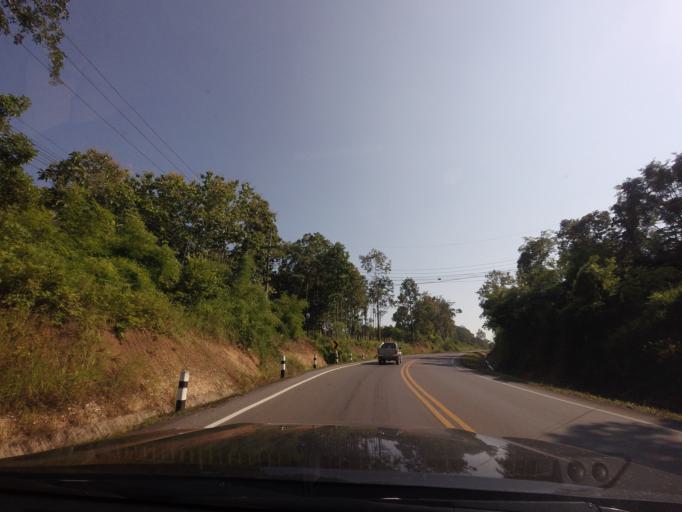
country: TH
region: Nan
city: Nan
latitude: 18.8293
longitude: 100.8089
